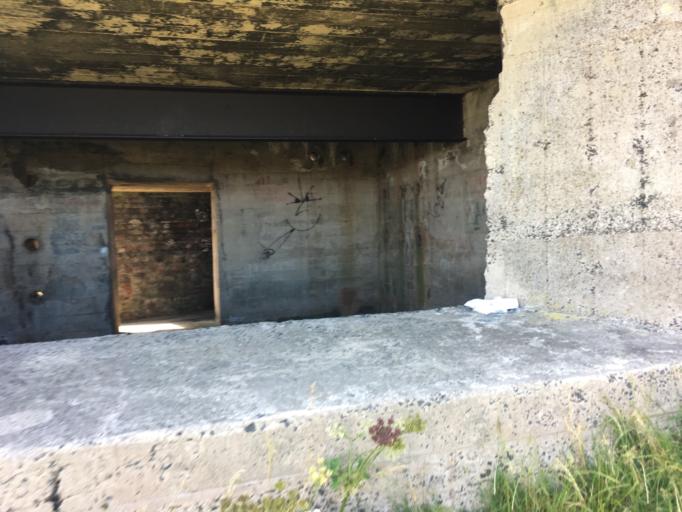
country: GB
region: England
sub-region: Northumberland
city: Ancroft
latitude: 55.7262
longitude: -1.9509
